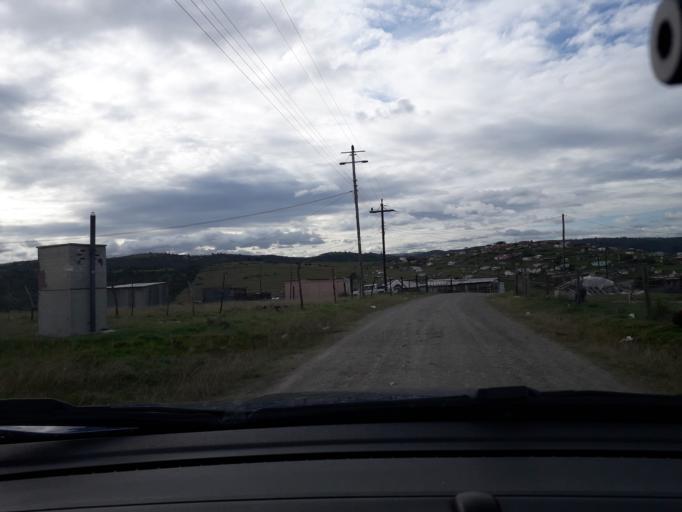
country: ZA
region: Eastern Cape
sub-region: Buffalo City Metropolitan Municipality
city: East London
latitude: -32.8516
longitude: 27.9837
